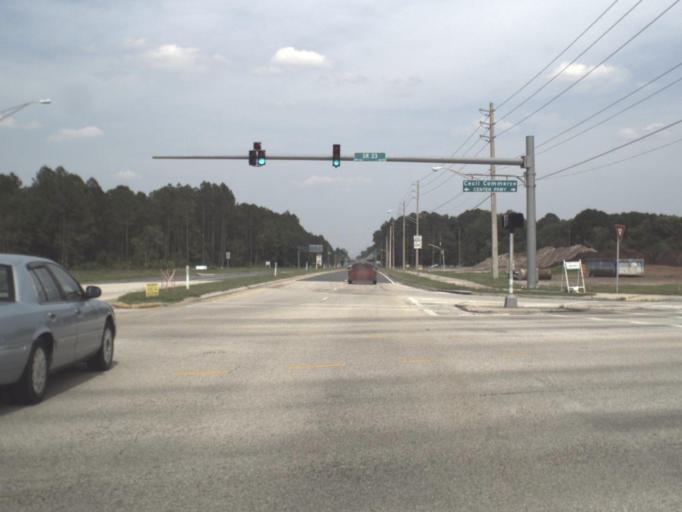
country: US
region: Florida
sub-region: Clay County
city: Bellair-Meadowbrook Terrace
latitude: 30.2469
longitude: -81.8459
